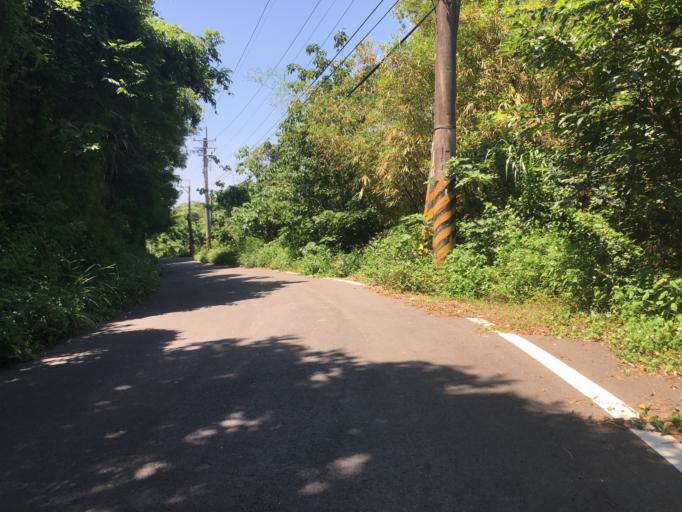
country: TW
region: Taiwan
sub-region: Hsinchu
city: Hsinchu
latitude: 24.7328
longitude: 120.9804
